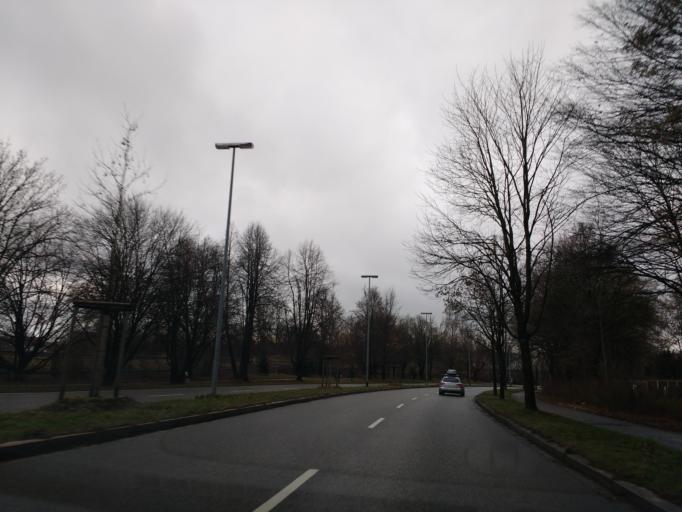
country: DE
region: Bavaria
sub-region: Swabia
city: Kempten (Allgaeu)
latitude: 47.7172
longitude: 10.3297
